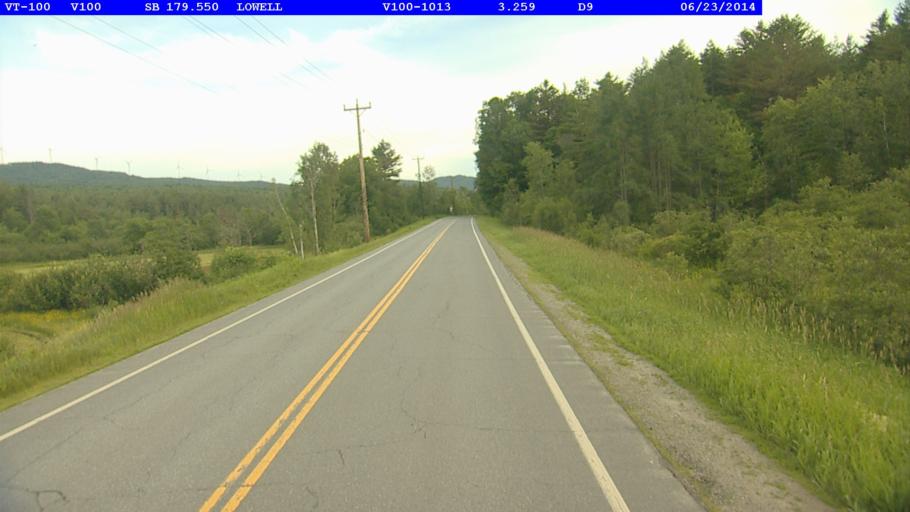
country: US
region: Vermont
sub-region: Lamoille County
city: Hyde Park
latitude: 44.7831
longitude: -72.4501
